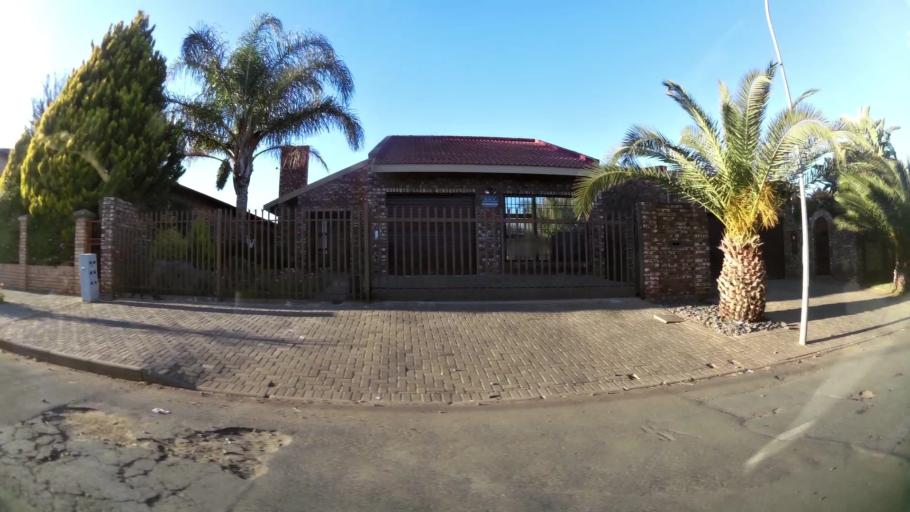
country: ZA
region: Northern Cape
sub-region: Frances Baard District Municipality
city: Kimberley
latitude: -28.7523
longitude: 24.7415
